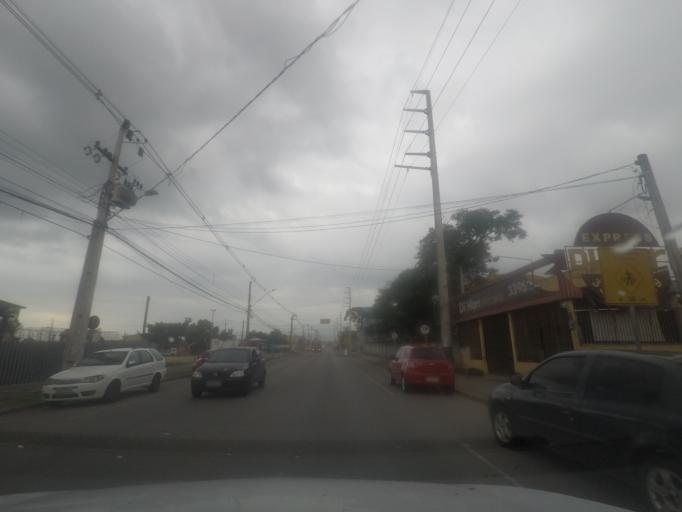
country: BR
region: Parana
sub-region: Sao Jose Dos Pinhais
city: Sao Jose dos Pinhais
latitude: -25.5547
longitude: -49.2523
